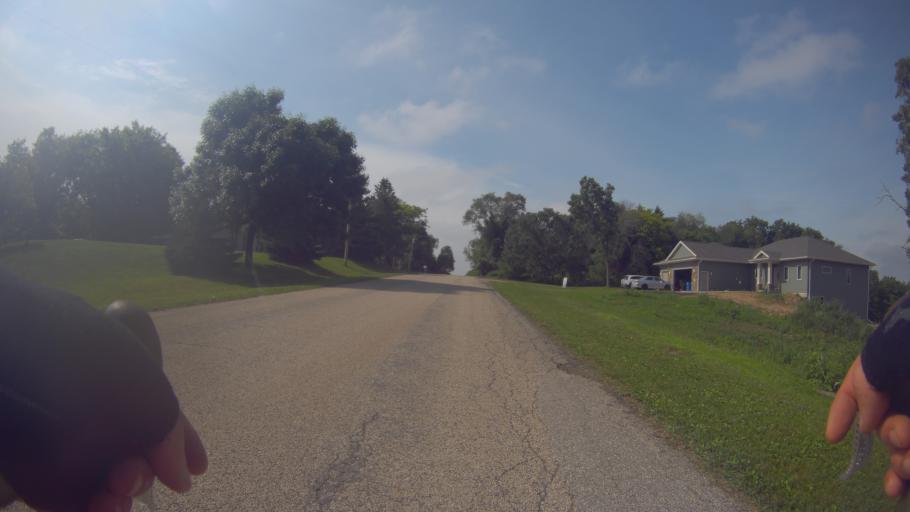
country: US
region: Wisconsin
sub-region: Dane County
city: Stoughton
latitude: 42.9903
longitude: -89.1904
